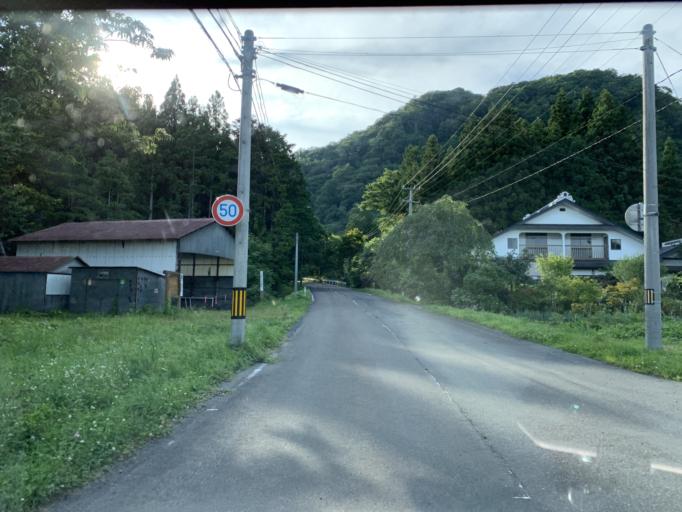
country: JP
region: Iwate
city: Ichinoseki
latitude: 38.9028
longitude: 140.9294
